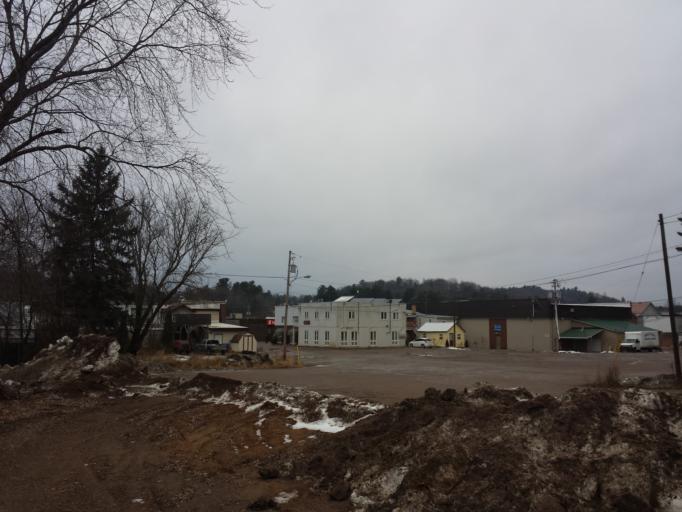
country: CA
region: Ontario
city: Bancroft
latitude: 45.0578
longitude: -77.8525
